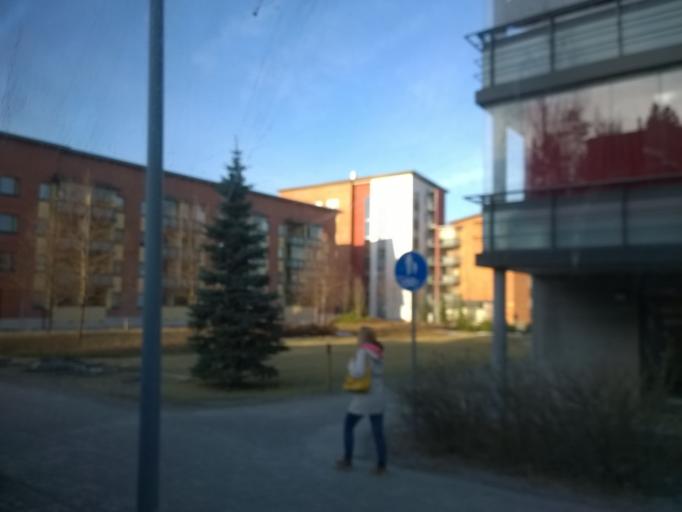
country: FI
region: Pirkanmaa
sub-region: Tampere
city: Tampere
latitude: 61.4490
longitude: 23.8513
